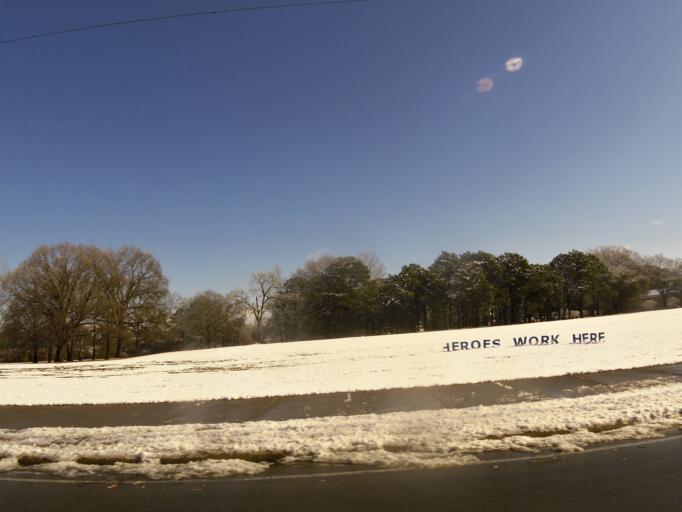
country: US
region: North Carolina
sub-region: Wilson County
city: Wilson
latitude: 35.7259
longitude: -77.8963
